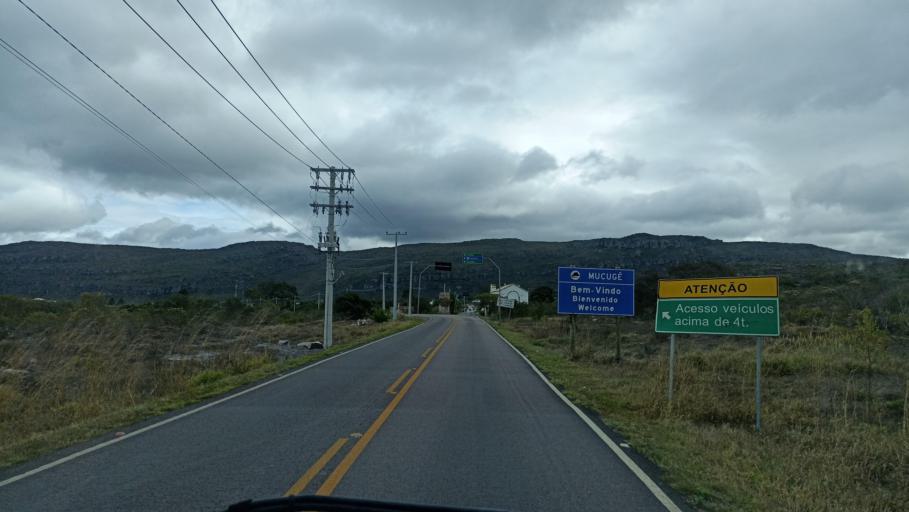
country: BR
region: Bahia
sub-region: Andarai
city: Vera Cruz
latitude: -13.0013
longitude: -41.3647
